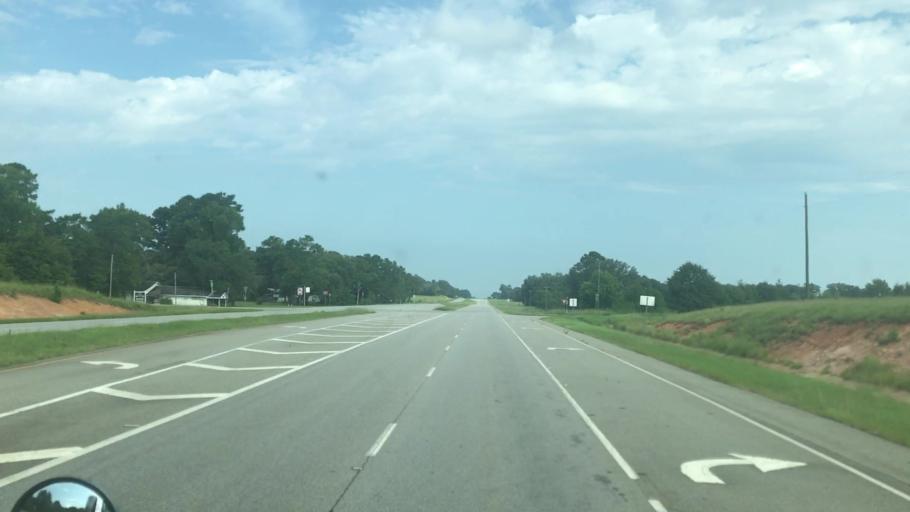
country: US
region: Georgia
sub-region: Early County
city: Blakely
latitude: 31.3029
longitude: -84.8625
